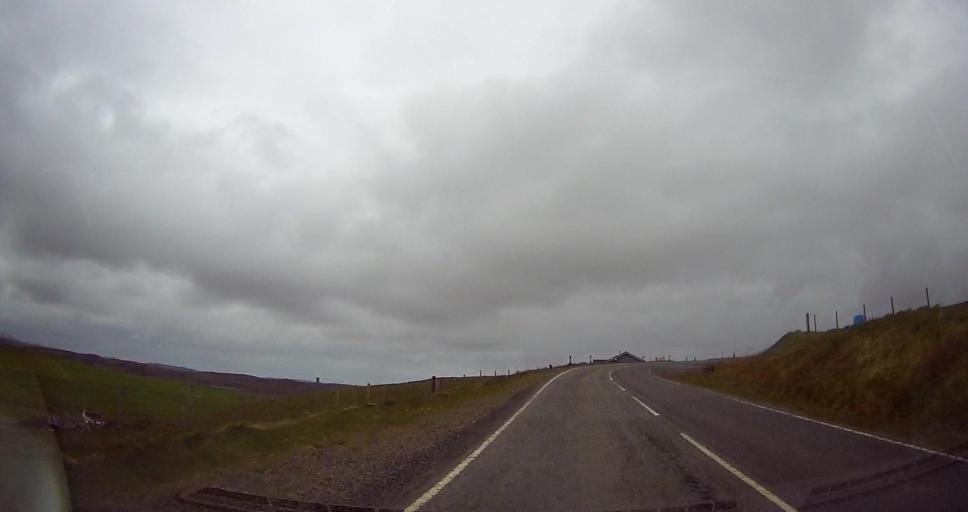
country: GB
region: Scotland
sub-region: Shetland Islands
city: Lerwick
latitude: 60.2574
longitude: -1.4077
